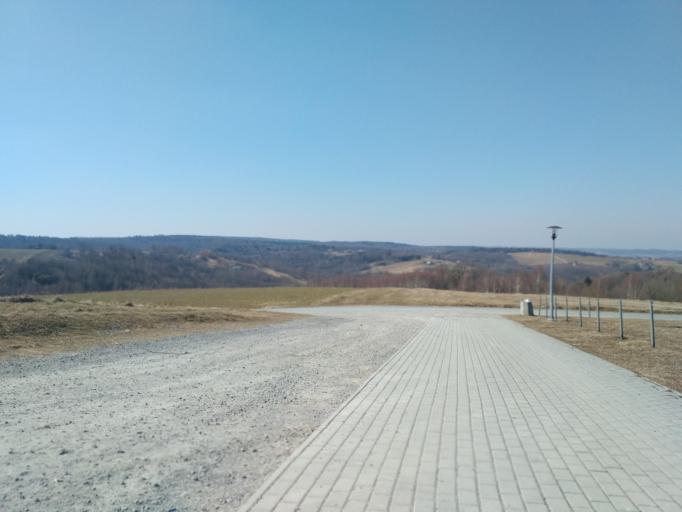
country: PL
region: Subcarpathian Voivodeship
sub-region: Powiat strzyzowski
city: Czudec
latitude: 49.9801
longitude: 21.8396
